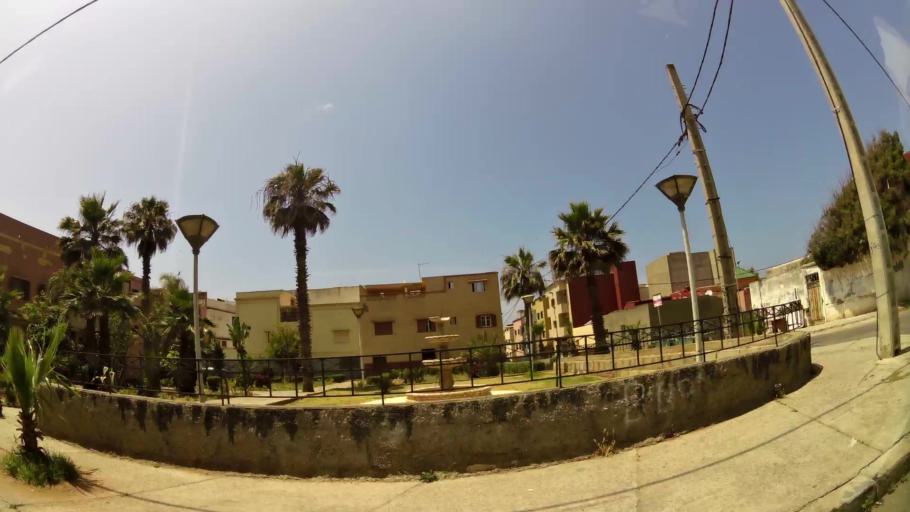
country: MA
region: Rabat-Sale-Zemmour-Zaer
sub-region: Rabat
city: Rabat
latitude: 34.0120
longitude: -6.8610
